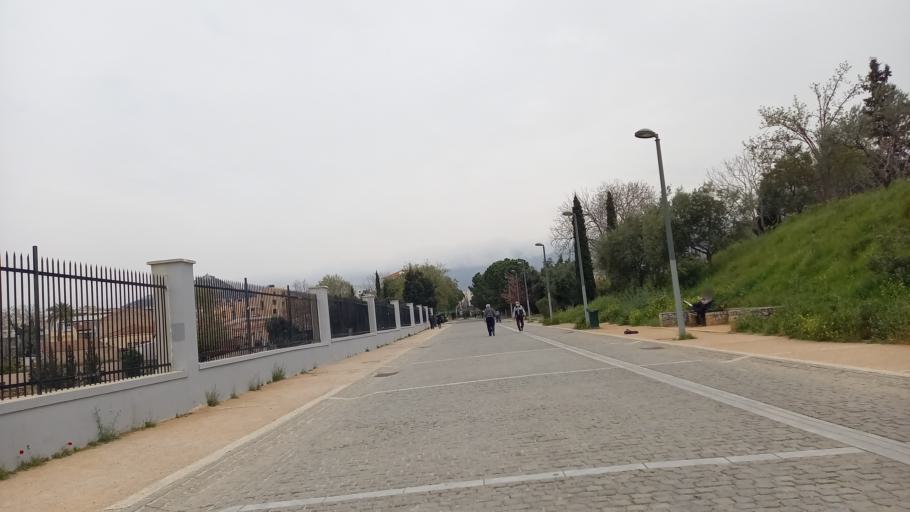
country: GR
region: Attica
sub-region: Nomarchia Athinas
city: Athens
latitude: 37.9779
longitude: 23.7178
